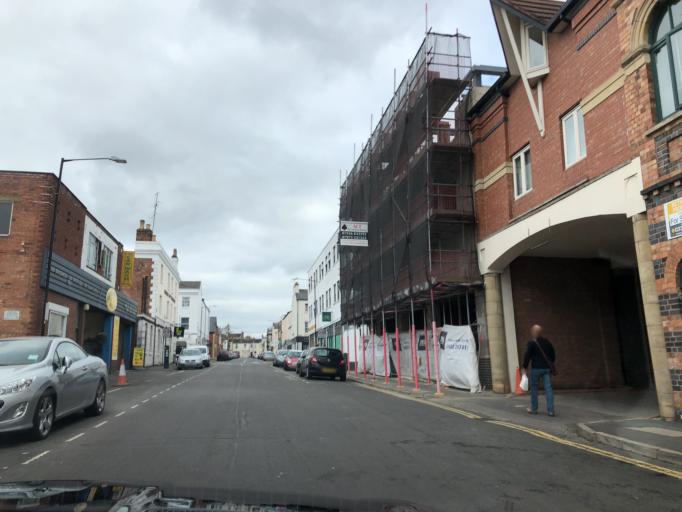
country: GB
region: England
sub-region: Warwickshire
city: Royal Leamington Spa
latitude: 52.2915
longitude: -1.5325
